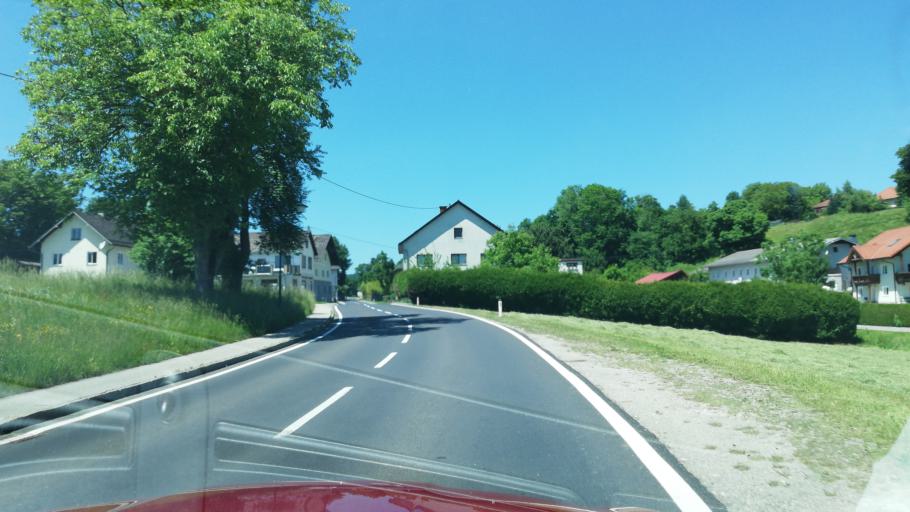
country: AT
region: Upper Austria
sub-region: Politischer Bezirk Vocklabruck
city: Niederthalheim
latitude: 48.1010
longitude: 13.7661
